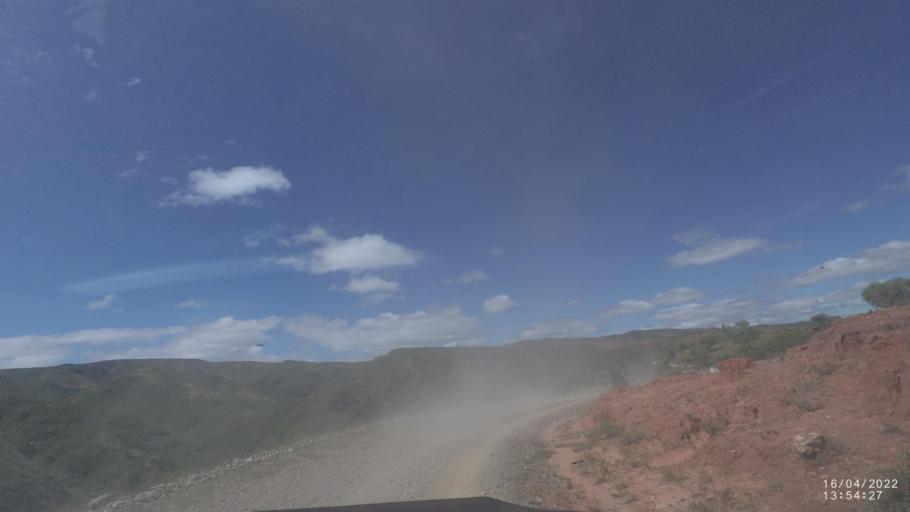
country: BO
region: Cochabamba
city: Mizque
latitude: -18.0258
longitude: -65.5656
